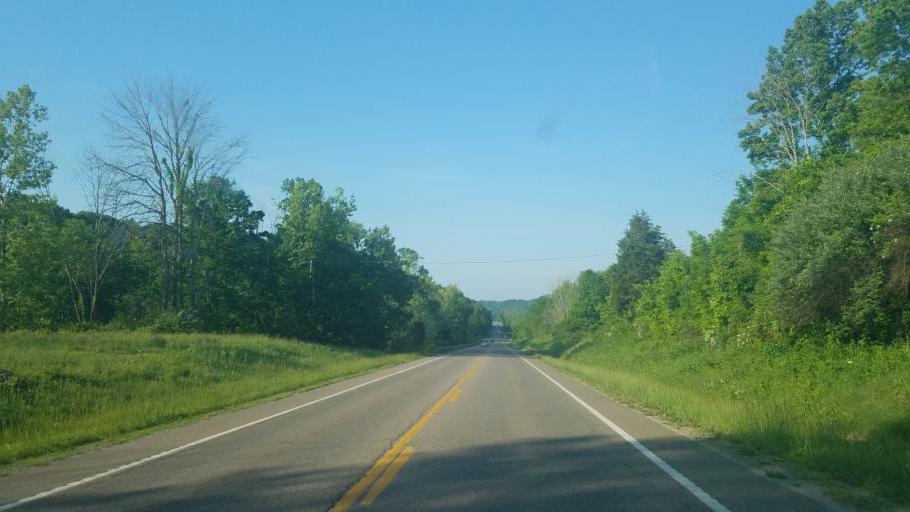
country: US
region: West Virginia
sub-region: Mason County
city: New Haven
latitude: 39.1142
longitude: -81.9161
